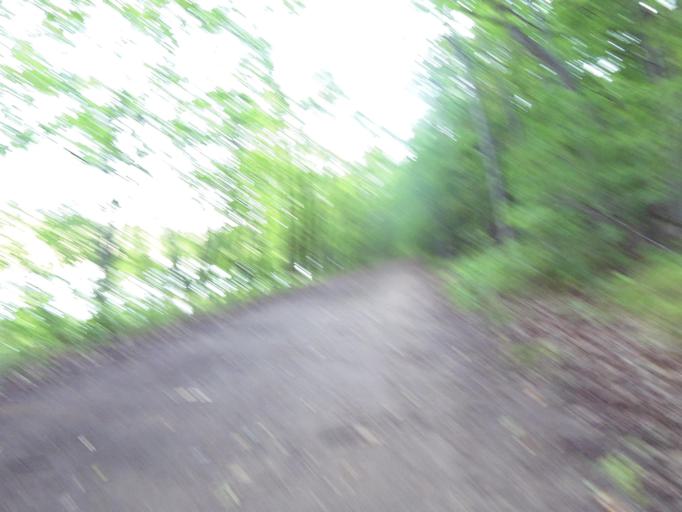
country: US
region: Minnesota
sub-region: Washington County
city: Afton
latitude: 44.8446
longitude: -92.7702
